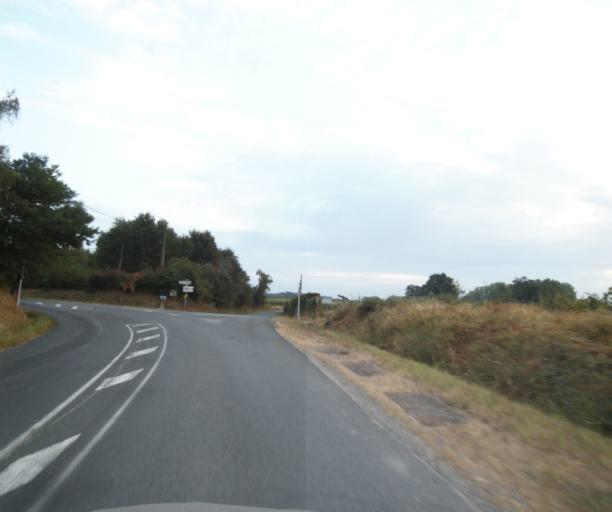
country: FR
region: Aquitaine
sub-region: Departement de la Gironde
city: La Sauve
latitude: 44.7564
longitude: -0.3285
